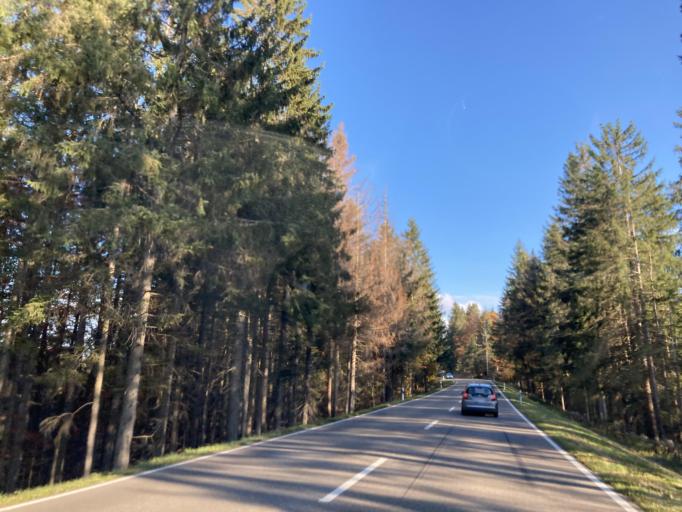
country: DE
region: Baden-Wuerttemberg
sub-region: Freiburg Region
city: Gutenbach
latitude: 47.9916
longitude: 8.1576
